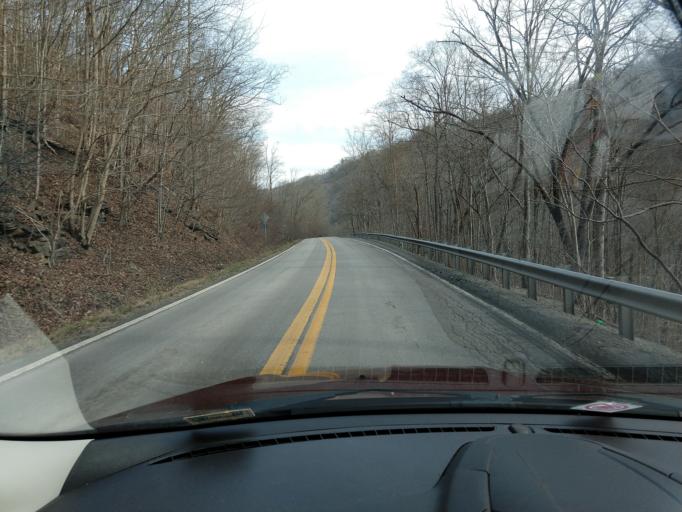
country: US
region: West Virginia
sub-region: McDowell County
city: Welch
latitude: 37.3180
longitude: -81.7162
